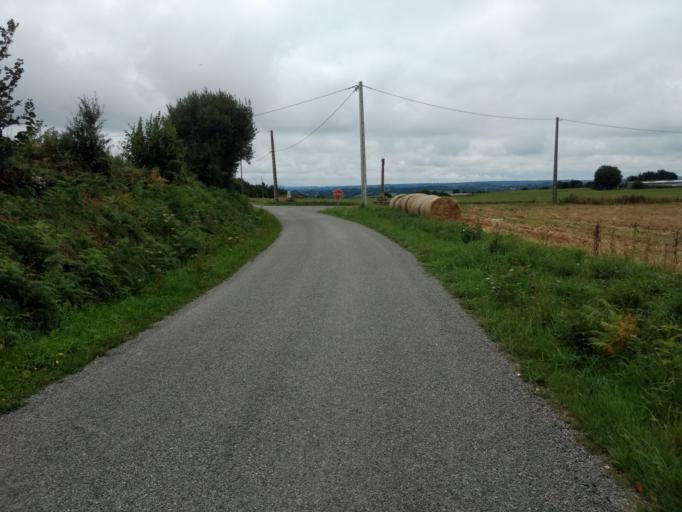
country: FR
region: Brittany
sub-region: Departement du Finistere
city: Loperhet
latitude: 48.3653
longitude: -4.2900
